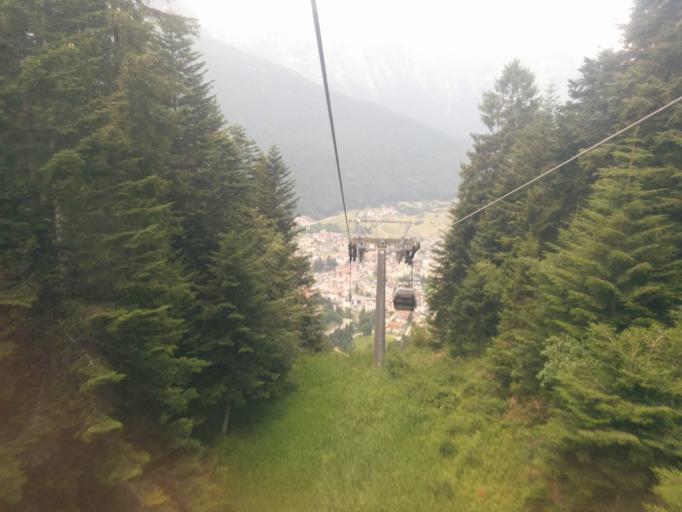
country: IT
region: Trentino-Alto Adige
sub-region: Provincia di Trento
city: Andalo
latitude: 46.1557
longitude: 11.0125
